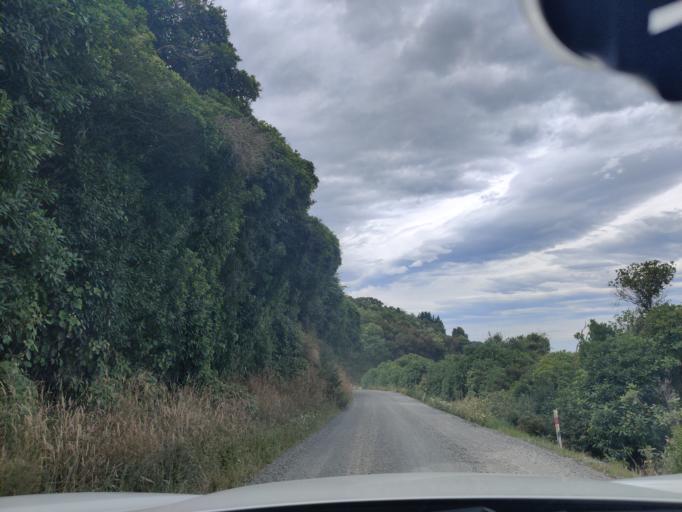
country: NZ
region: Wellington
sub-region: Masterton District
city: Masterton
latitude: -41.0410
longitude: 175.4092
